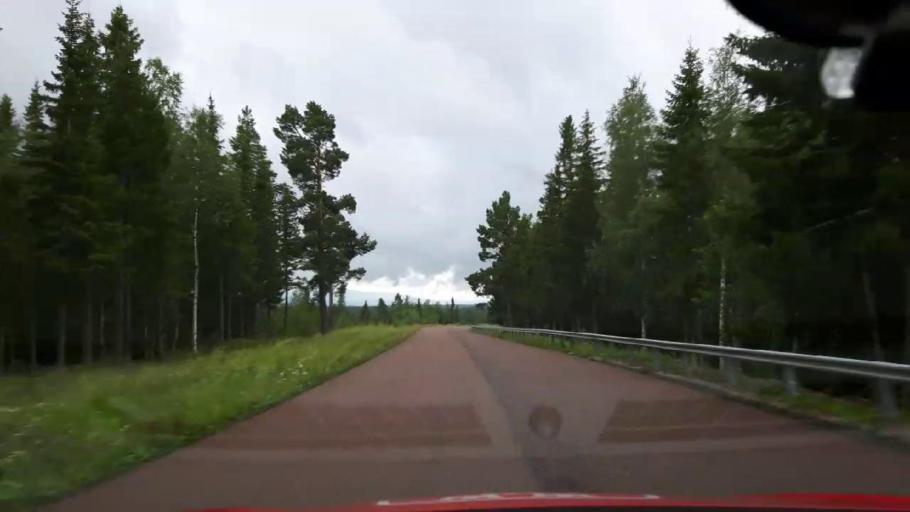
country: SE
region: Jaemtland
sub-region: Krokoms Kommun
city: Valla
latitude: 63.3523
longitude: 13.7240
